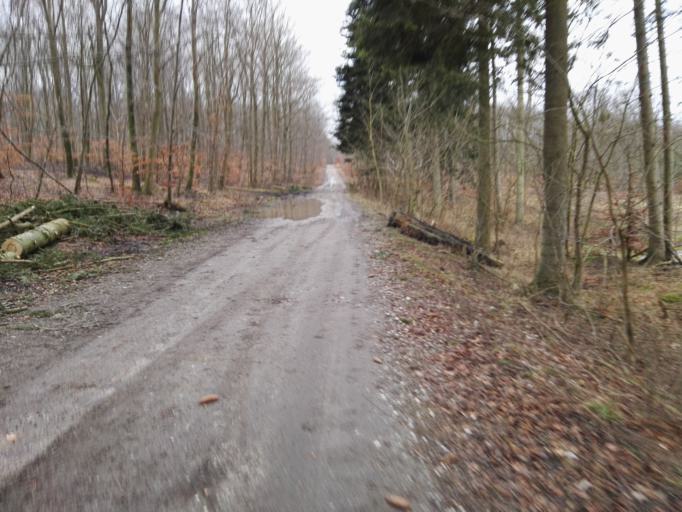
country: DK
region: Zealand
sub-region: Lejre Kommune
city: Lejre
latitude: 55.6442
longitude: 11.9304
